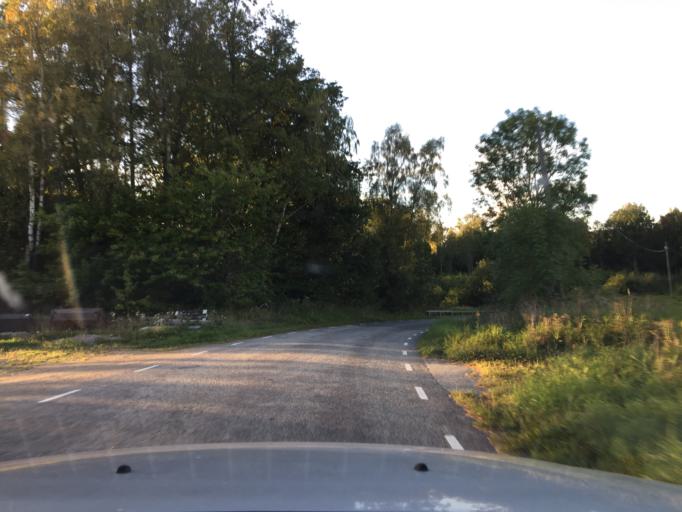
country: SE
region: Skane
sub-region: Hassleholms Kommun
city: Sosdala
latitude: 55.9740
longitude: 13.7442
